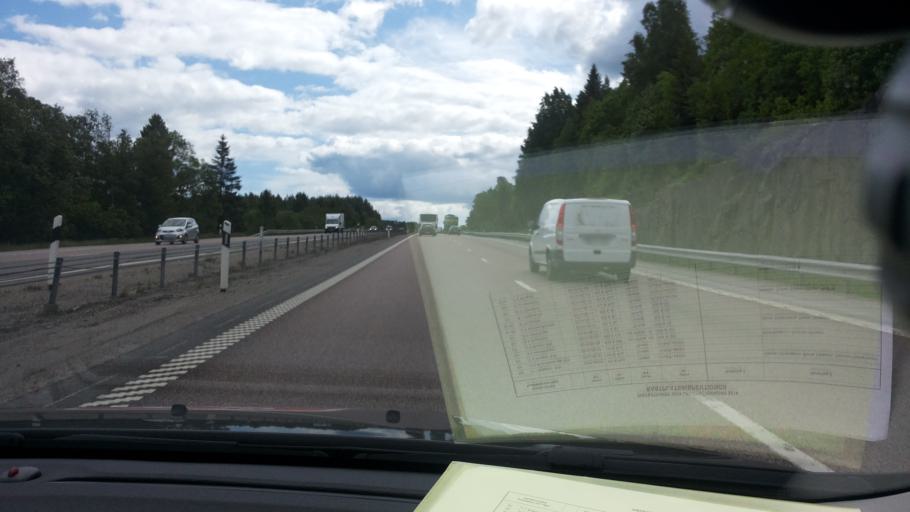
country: SE
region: Vaesternorrland
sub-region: Sundsvalls Kommun
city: Sundsbruk
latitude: 62.4363
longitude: 17.3390
